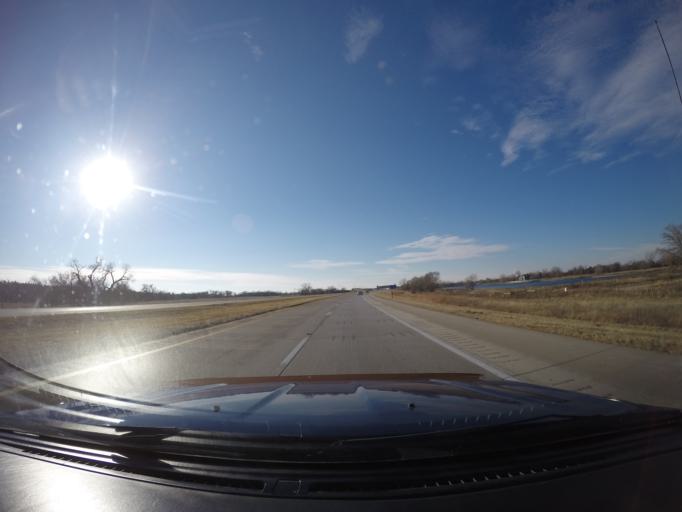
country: US
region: Nebraska
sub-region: Buffalo County
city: Kearney
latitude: 40.6701
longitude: -99.0177
